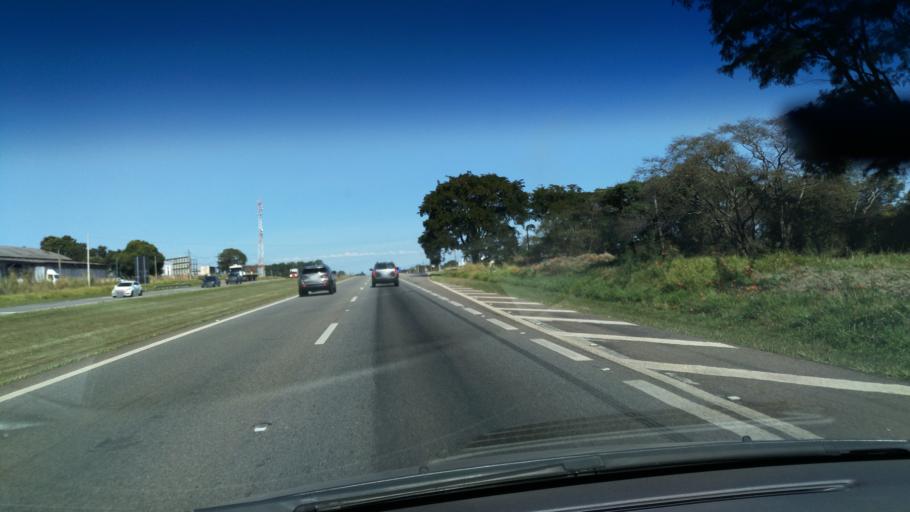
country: BR
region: Sao Paulo
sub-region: Mogi-Mirim
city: Mogi Mirim
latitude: -22.4636
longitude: -46.9822
